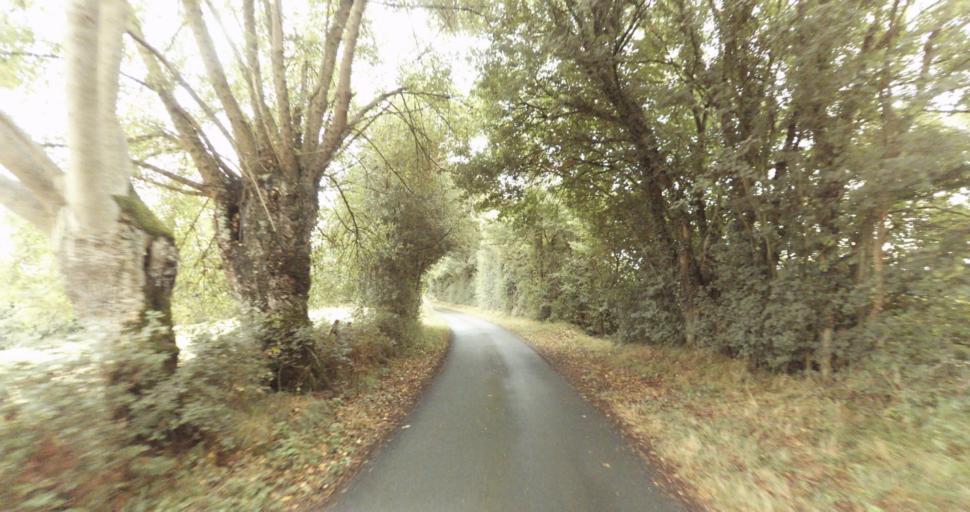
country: FR
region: Lower Normandy
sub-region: Departement de l'Orne
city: Vimoutiers
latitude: 48.9096
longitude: 0.1674
